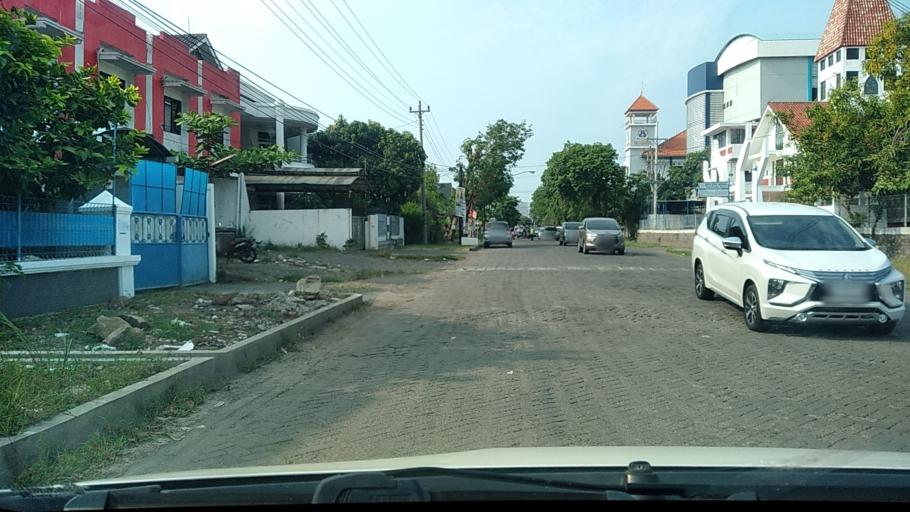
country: ID
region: Central Java
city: Semarang
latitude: -6.9657
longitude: 110.3961
